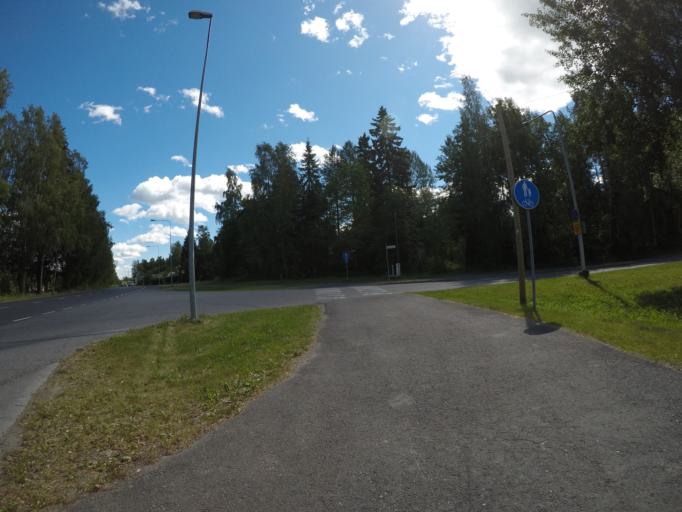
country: FI
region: Haeme
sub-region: Haemeenlinna
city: Haemeenlinna
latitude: 61.0196
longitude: 24.4262
